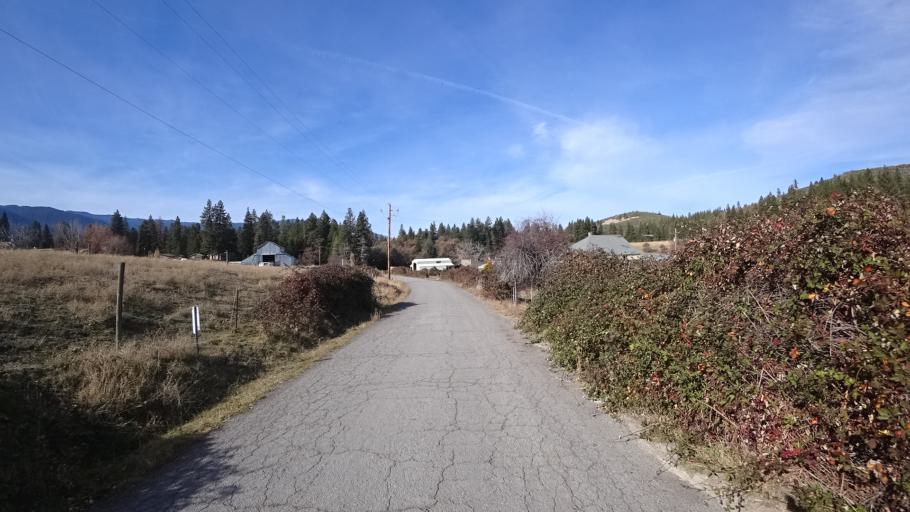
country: US
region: California
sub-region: Siskiyou County
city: Weed
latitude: 41.4332
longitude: -122.4086
